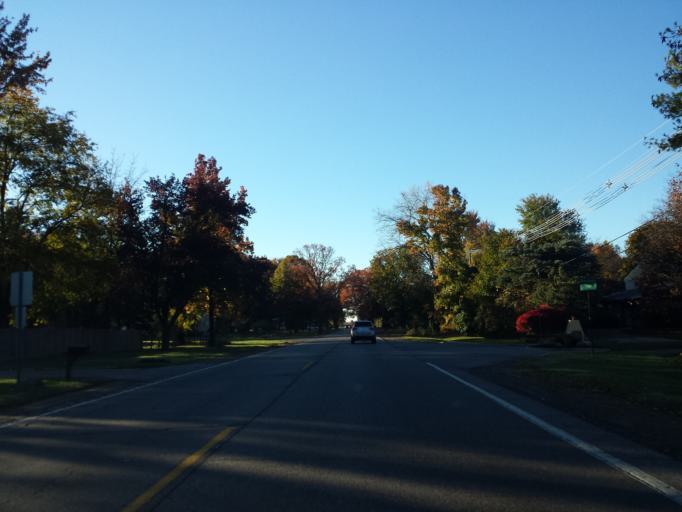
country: US
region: Michigan
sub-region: Oakland County
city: Lathrup Village
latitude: 42.5091
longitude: -83.2423
